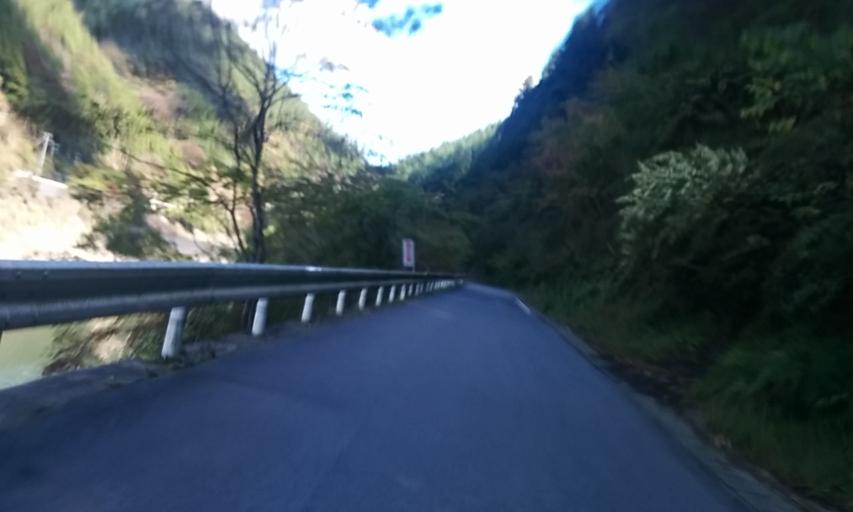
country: JP
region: Kyoto
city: Kameoka
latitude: 35.1280
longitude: 135.5695
